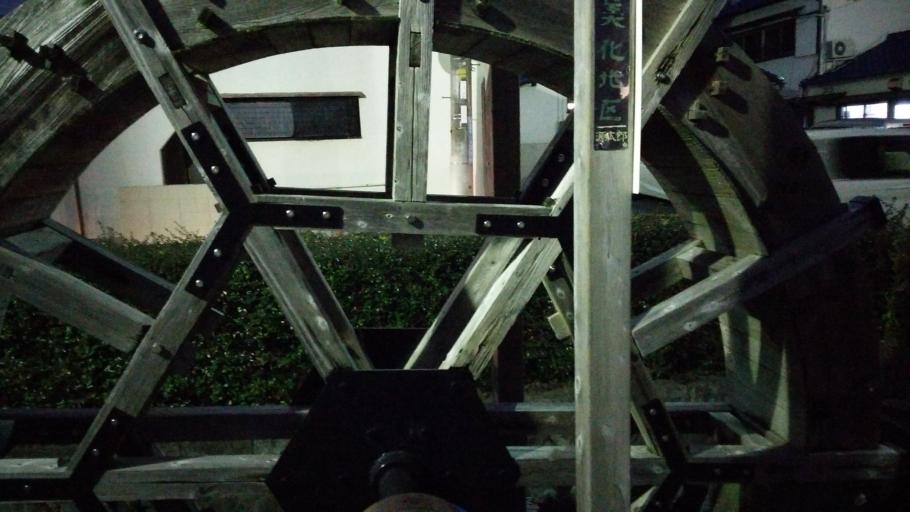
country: JP
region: Hyogo
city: Itami
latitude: 34.7637
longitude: 135.3804
